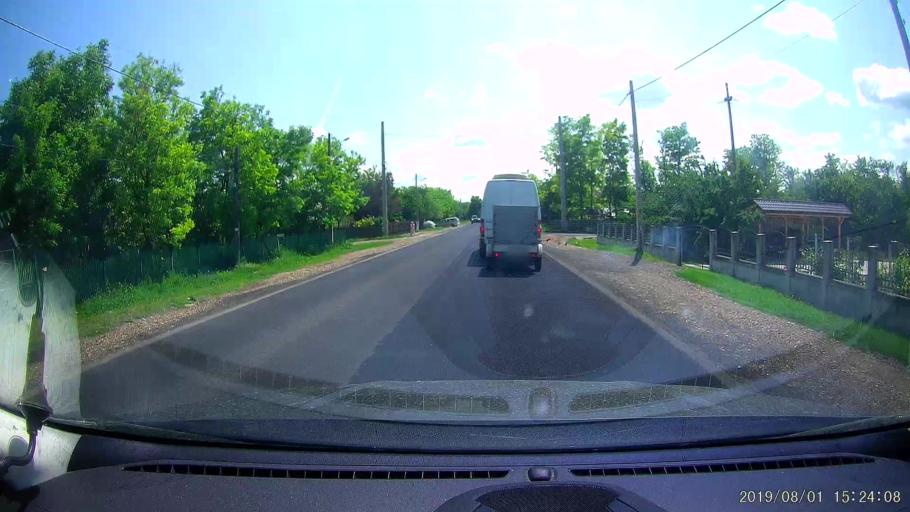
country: RO
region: Braila
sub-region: Comuna Viziru
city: Lanurile
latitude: 45.0351
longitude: 27.7521
